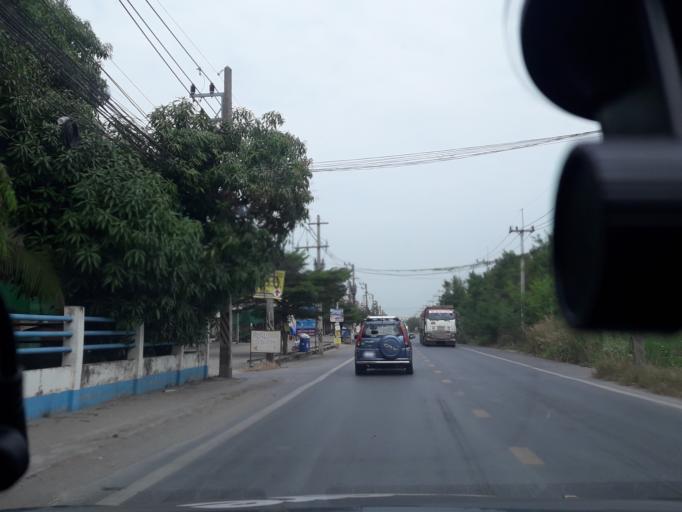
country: TH
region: Pathum Thani
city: Ban Rangsit
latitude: 14.0207
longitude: 100.7535
